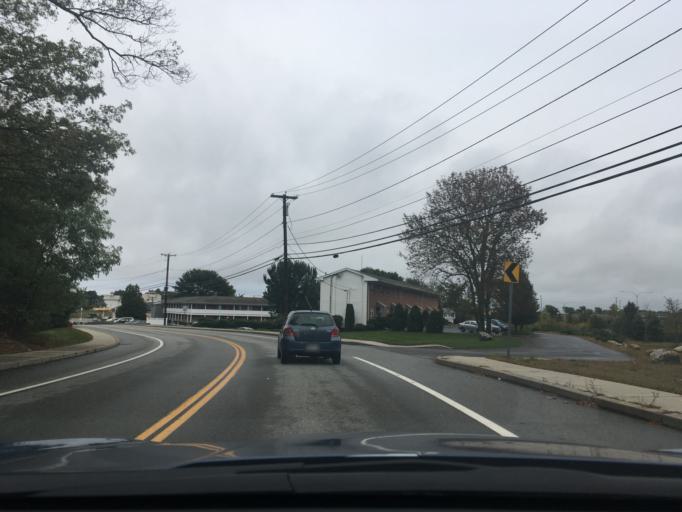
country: US
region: Rhode Island
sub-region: Kent County
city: East Greenwich
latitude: 41.6061
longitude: -71.4594
